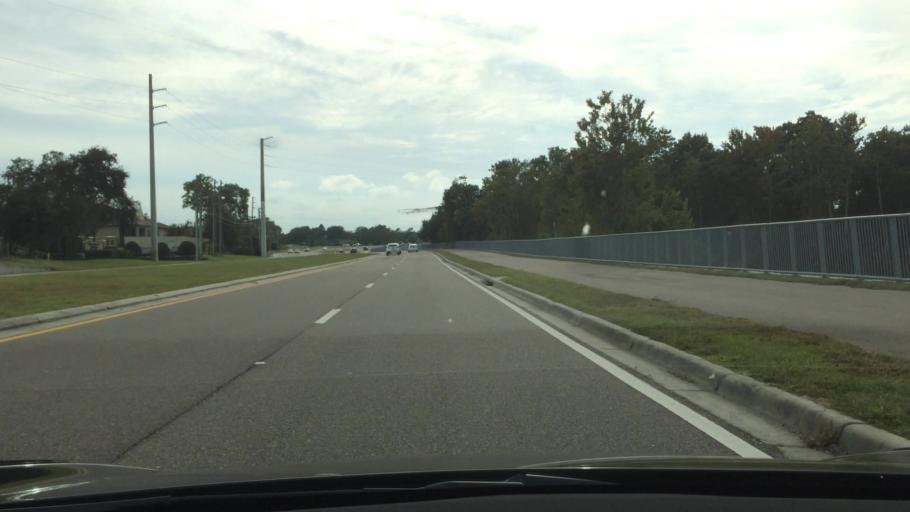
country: US
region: Florida
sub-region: Pinellas County
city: Tarpon Springs
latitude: 28.1509
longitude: -82.7286
